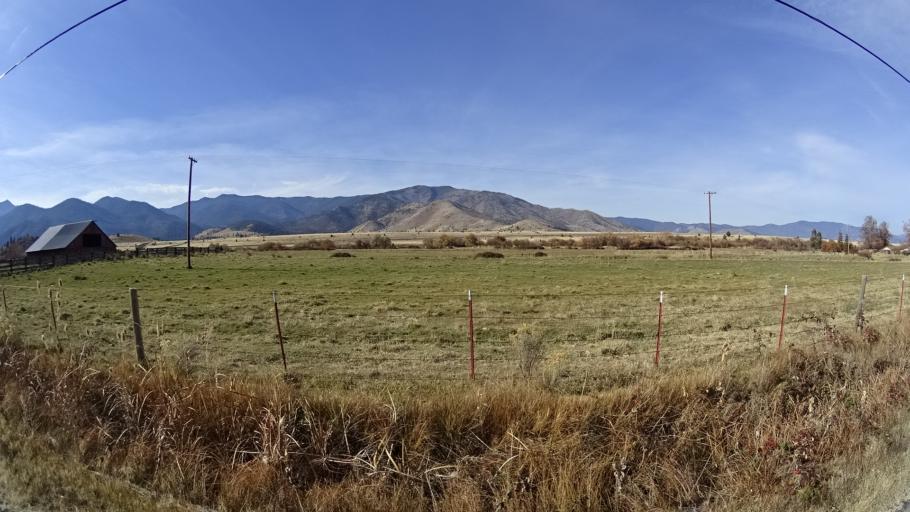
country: US
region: California
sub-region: Siskiyou County
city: Weed
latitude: 41.4630
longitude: -122.4339
